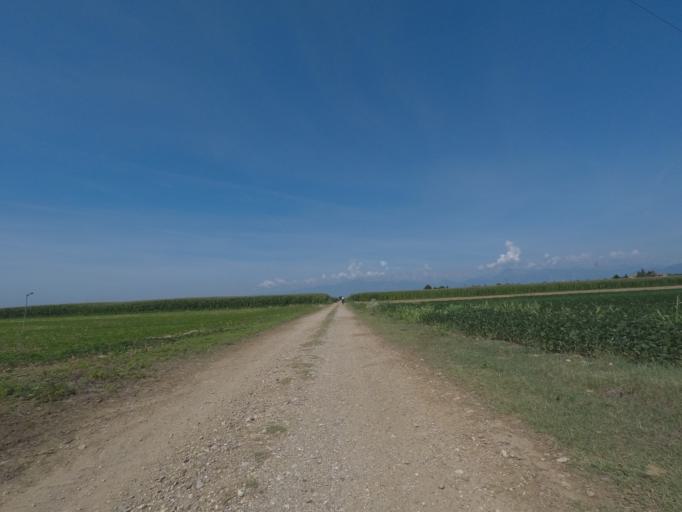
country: IT
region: Friuli Venezia Giulia
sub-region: Provincia di Udine
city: Flaibano
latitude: 46.0818
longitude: 12.9791
